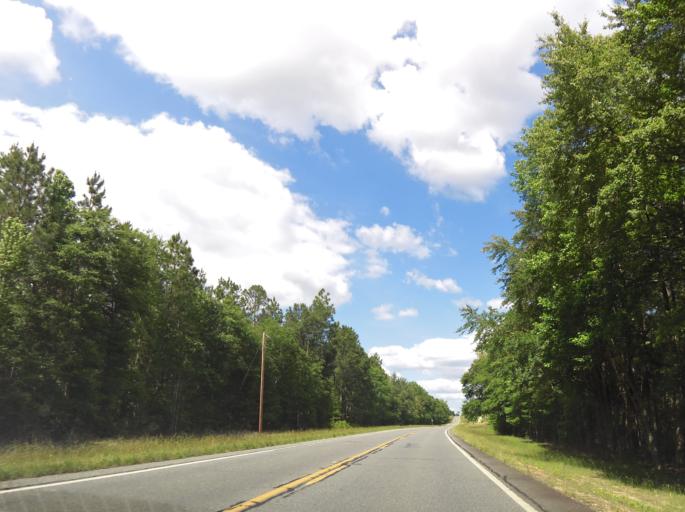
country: US
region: Georgia
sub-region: Treutlen County
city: Soperton
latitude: 32.3600
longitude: -82.6238
